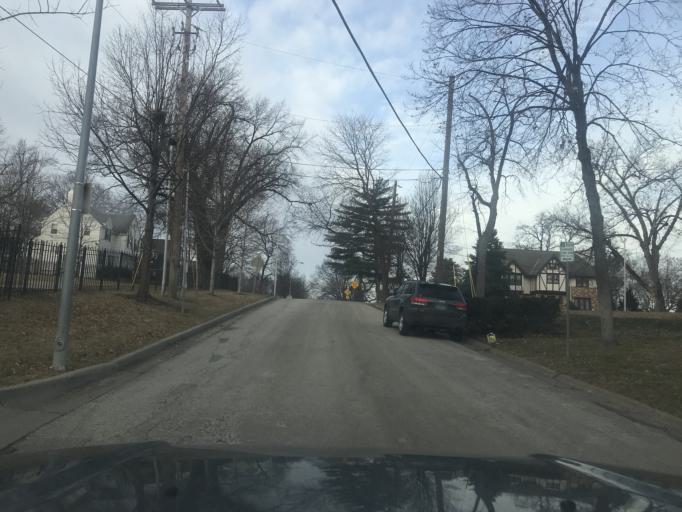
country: US
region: Kansas
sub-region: Johnson County
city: Westwood
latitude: 39.0370
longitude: -94.5937
